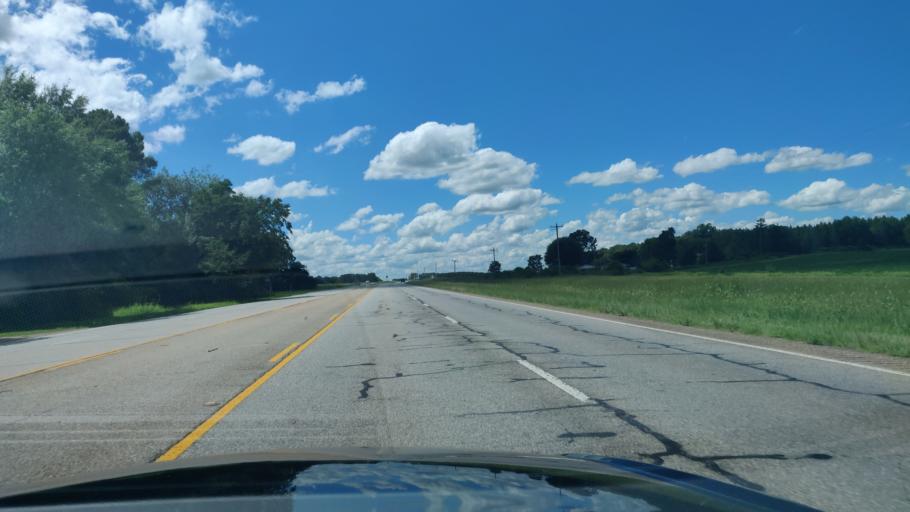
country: US
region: Georgia
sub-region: Stewart County
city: Richland
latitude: 31.9843
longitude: -84.6256
